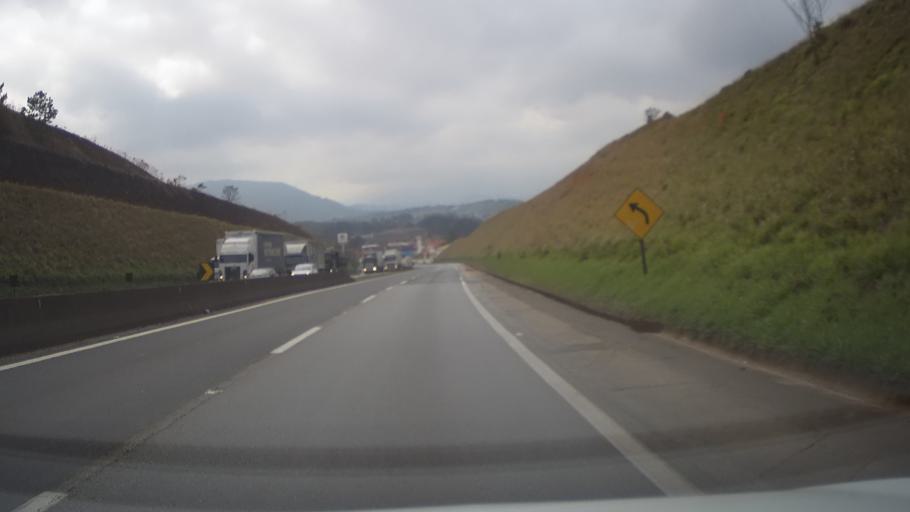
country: BR
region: Minas Gerais
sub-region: Extrema
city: Extrema
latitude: -22.8351
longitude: -46.3236
